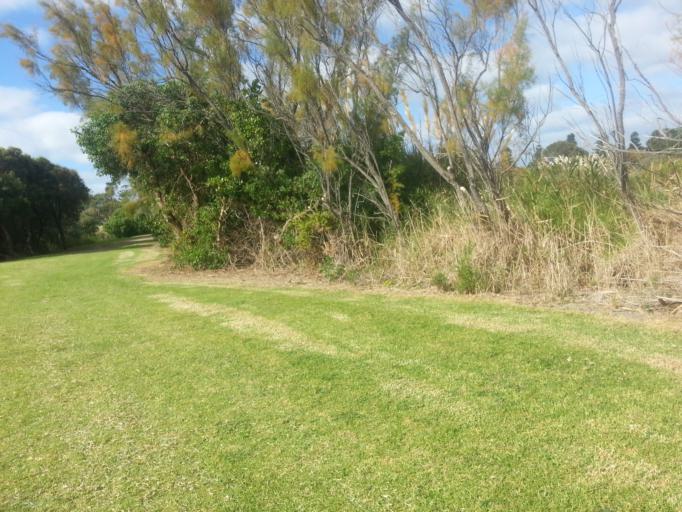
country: AU
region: Victoria
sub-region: Warrnambool
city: Warrnambool
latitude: -38.3916
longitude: 142.4769
